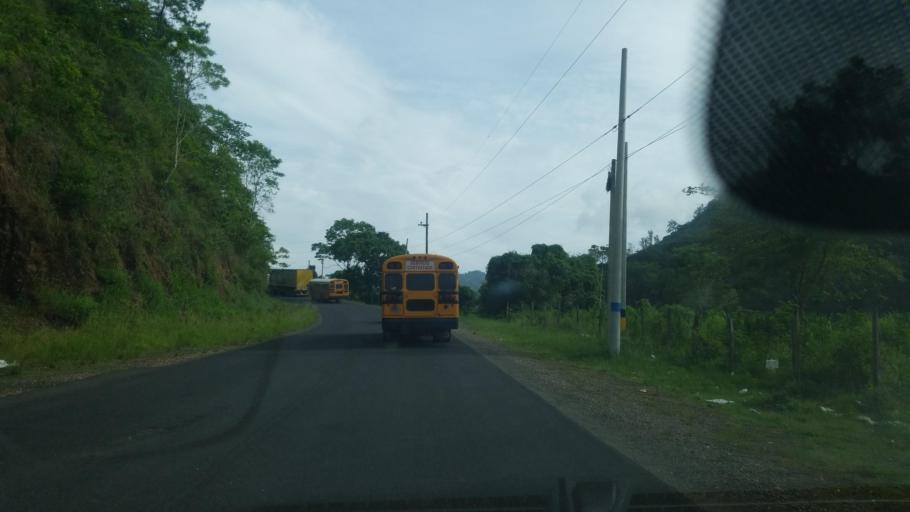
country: HN
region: Santa Barbara
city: Petoa
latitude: 15.2131
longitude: -88.2701
